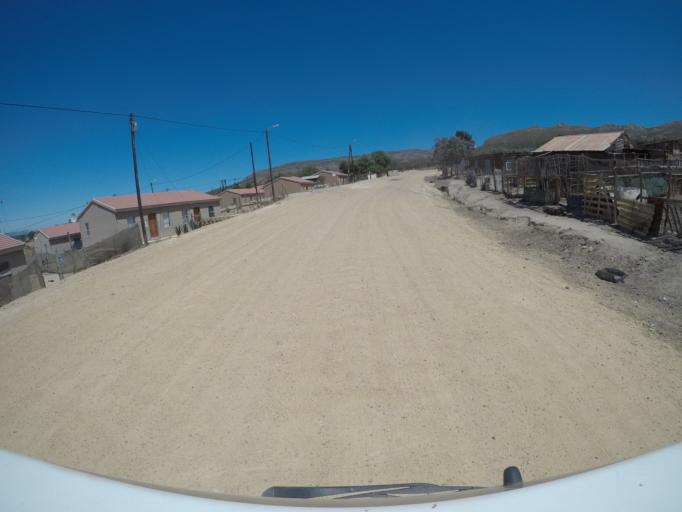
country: ZA
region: Western Cape
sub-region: Overberg District Municipality
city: Grabouw
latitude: -34.2227
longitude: 19.1924
